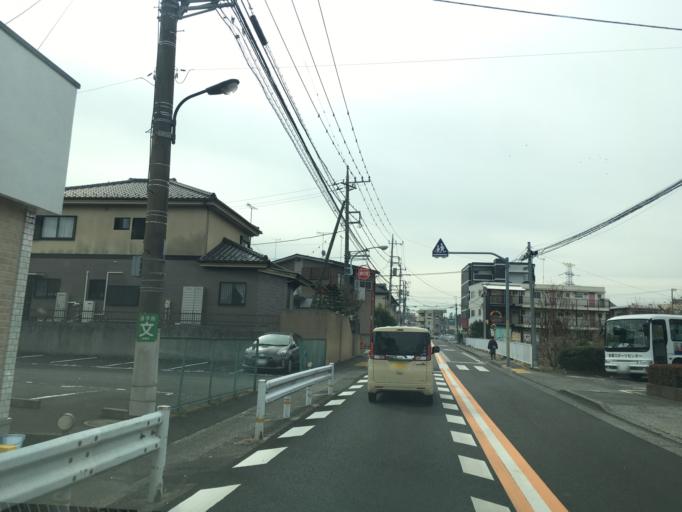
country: JP
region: Tokyo
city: Hino
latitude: 35.6420
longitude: 139.4378
